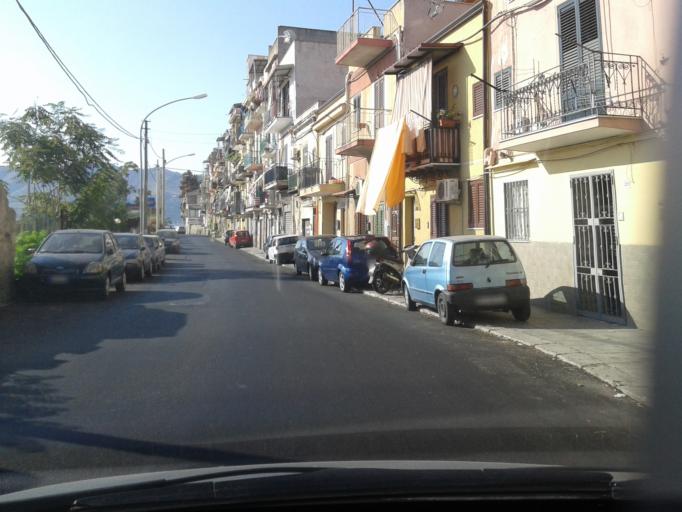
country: IT
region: Sicily
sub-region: Palermo
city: Piano dei Geli
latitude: 38.1083
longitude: 13.3089
